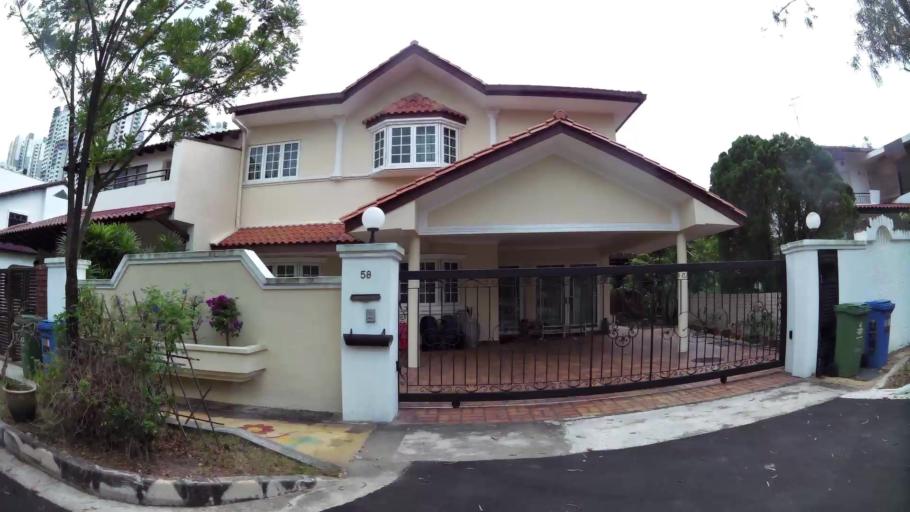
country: SG
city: Singapore
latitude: 1.3123
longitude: 103.7835
